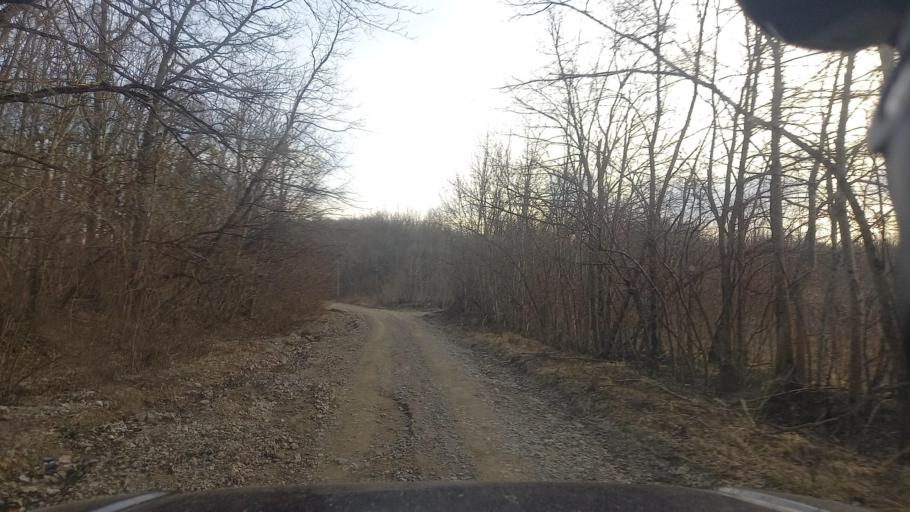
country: RU
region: Krasnodarskiy
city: Goryachiy Klyuch
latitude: 44.6907
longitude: 38.9779
